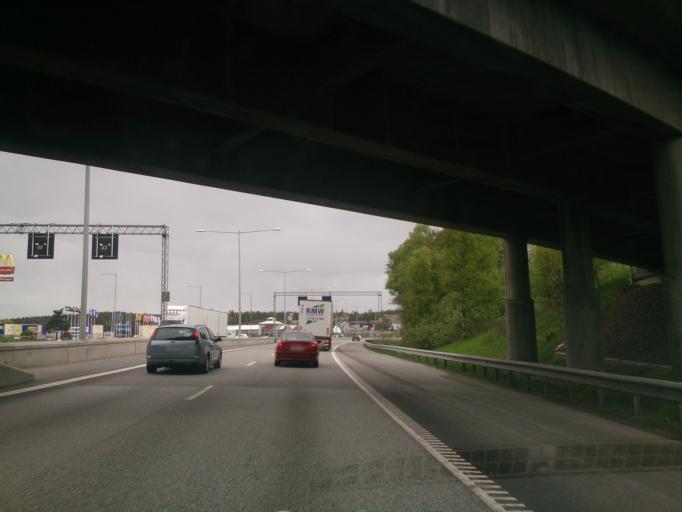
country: SE
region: Stockholm
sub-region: Sodertalje Kommun
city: Soedertaelje
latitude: 59.1991
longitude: 17.6627
